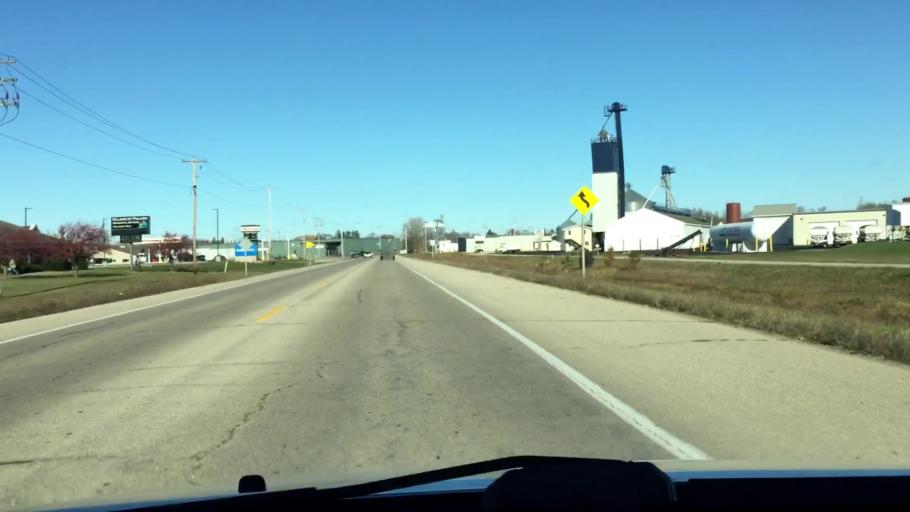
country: US
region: Wisconsin
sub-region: Brown County
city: Pulaski
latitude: 44.6646
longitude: -88.2271
